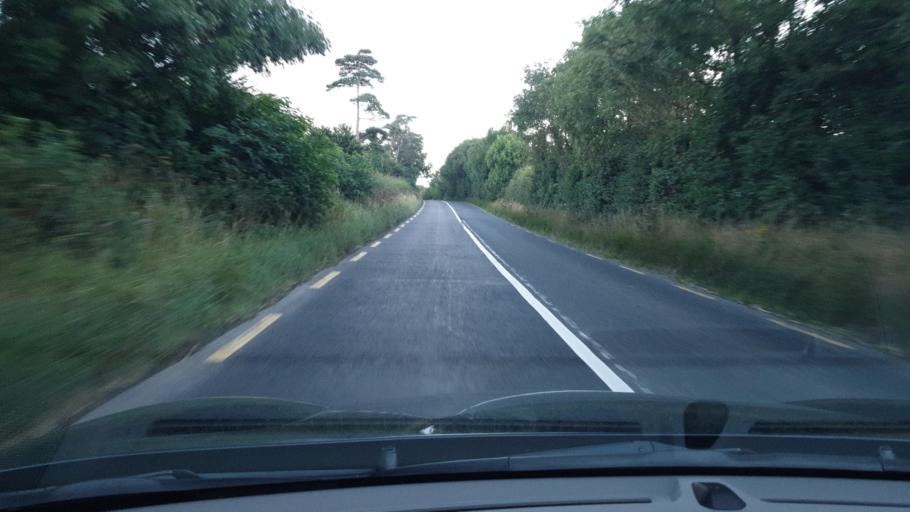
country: IE
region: Leinster
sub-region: Lu
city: Drogheda
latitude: 53.6909
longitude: -6.3758
